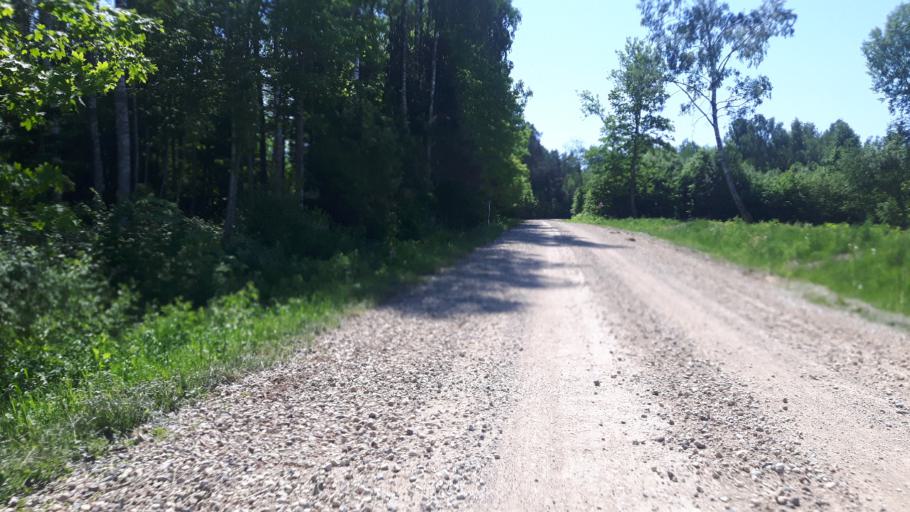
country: EE
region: Paernumaa
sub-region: Tootsi vald
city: Tootsi
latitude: 58.5102
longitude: 24.9085
